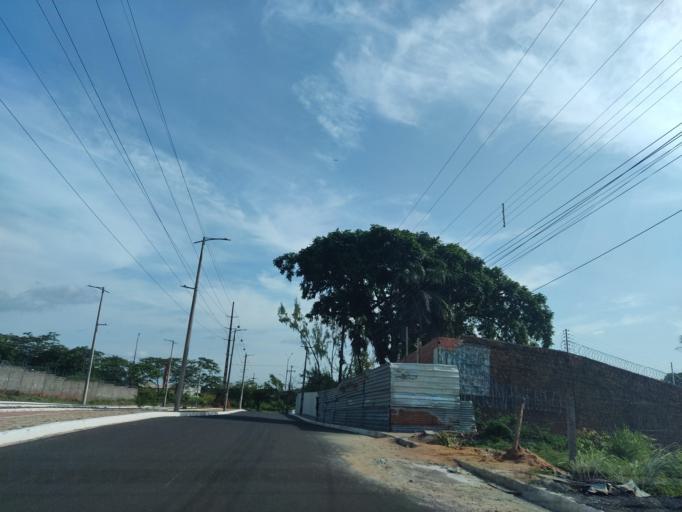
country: BR
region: Piaui
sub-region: Teresina
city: Teresina
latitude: -5.0774
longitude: -42.7516
